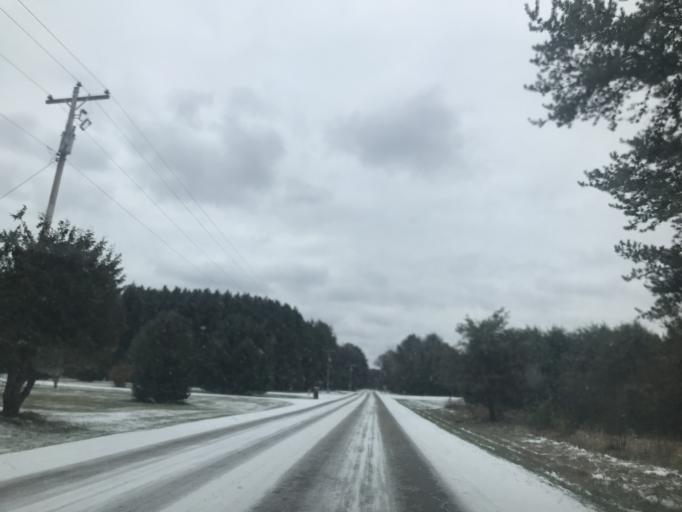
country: US
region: Wisconsin
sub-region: Marinette County
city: Marinette
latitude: 45.0557
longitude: -87.6583
